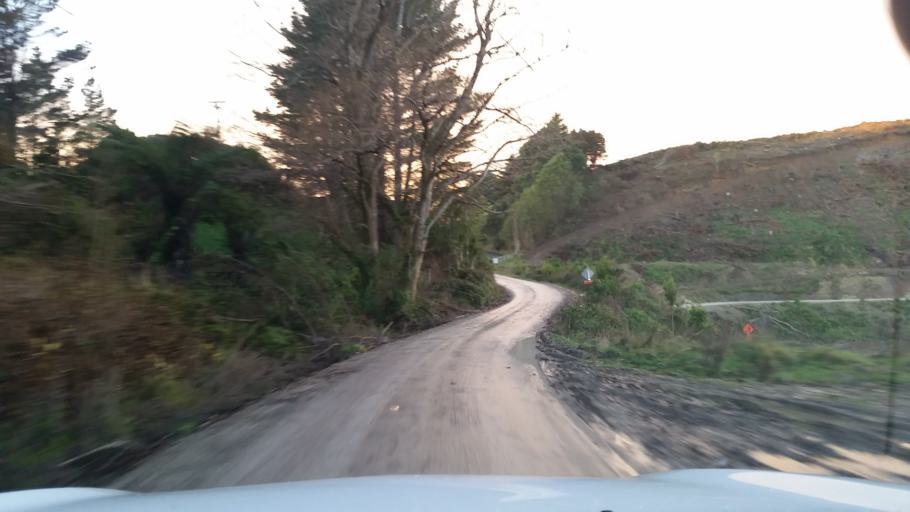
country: NZ
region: Manawatu-Wanganui
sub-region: Wanganui District
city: Wanganui
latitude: -39.7712
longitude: 174.8711
